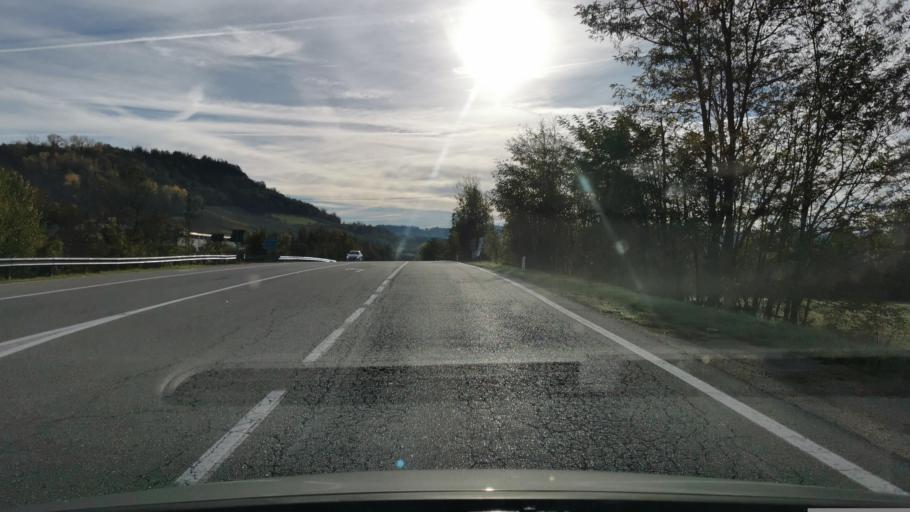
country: IT
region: Piedmont
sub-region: Provincia di Cuneo
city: Monchiero Borgonuovo
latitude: 44.5849
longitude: 7.9018
